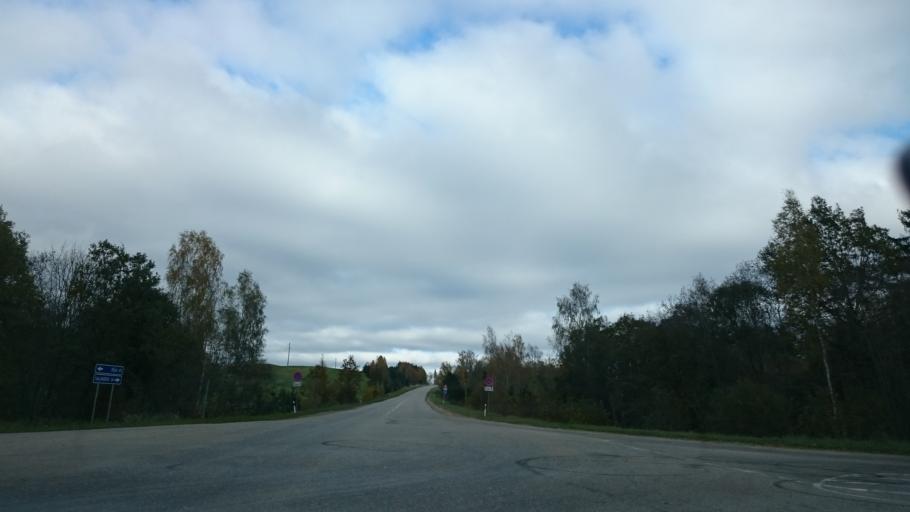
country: LV
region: Amatas Novads
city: Drabesi
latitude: 57.2608
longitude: 25.2677
